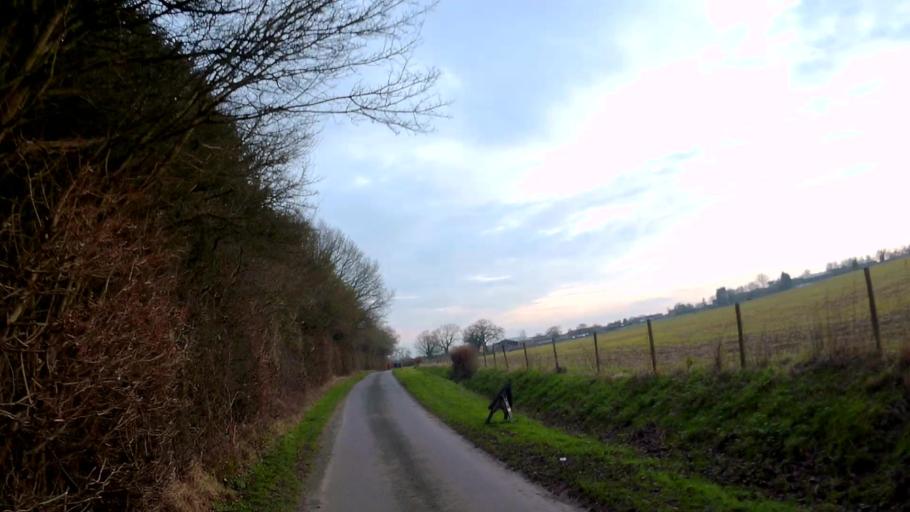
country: GB
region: England
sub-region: Lincolnshire
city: Bourne
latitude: 52.8181
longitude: -0.3995
